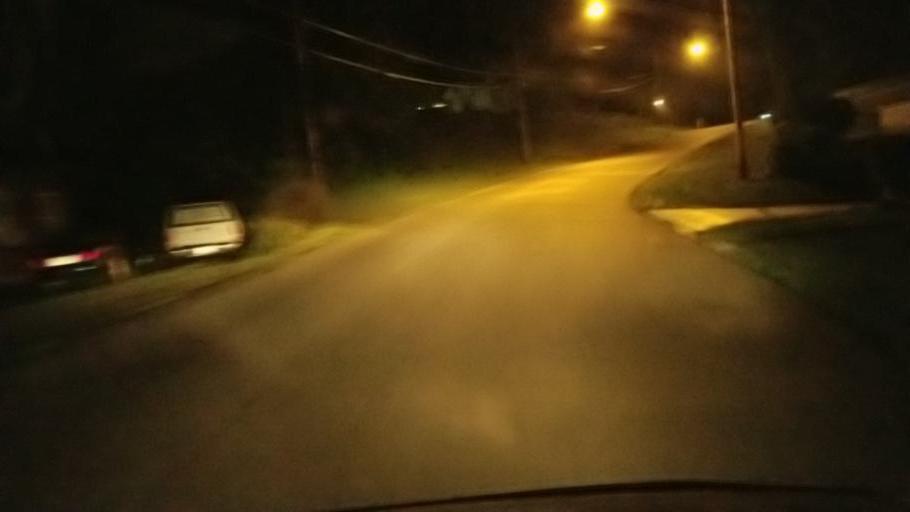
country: US
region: Ohio
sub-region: Coshocton County
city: Coshocton
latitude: 40.3369
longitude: -82.0064
